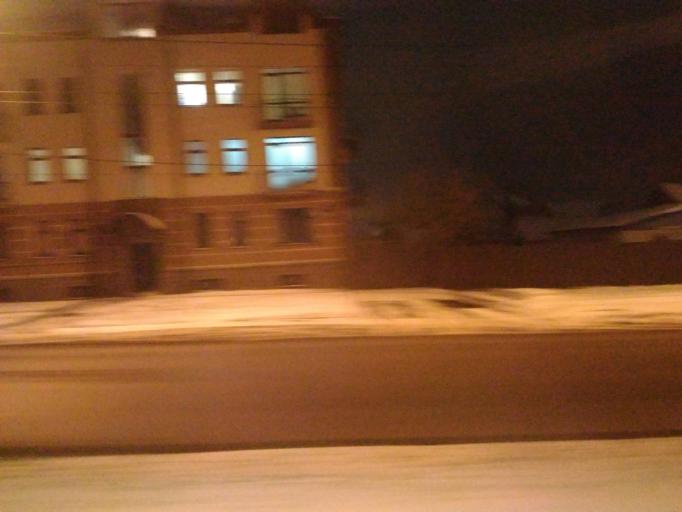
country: RU
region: Ulyanovsk
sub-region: Ulyanovskiy Rayon
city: Ulyanovsk
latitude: 54.3511
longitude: 48.3817
